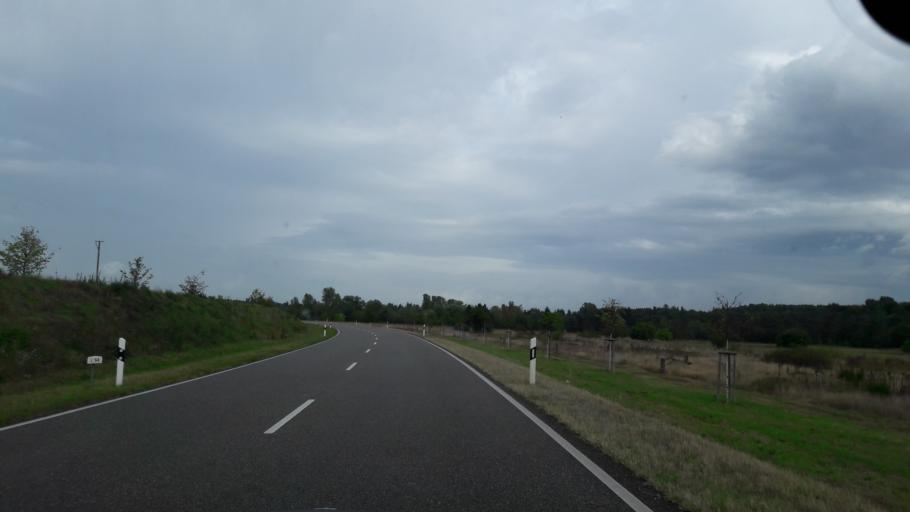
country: DE
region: Baden-Wuerttemberg
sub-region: Karlsruhe Region
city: Sankt Leon-Rot
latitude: 49.2569
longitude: 8.6458
